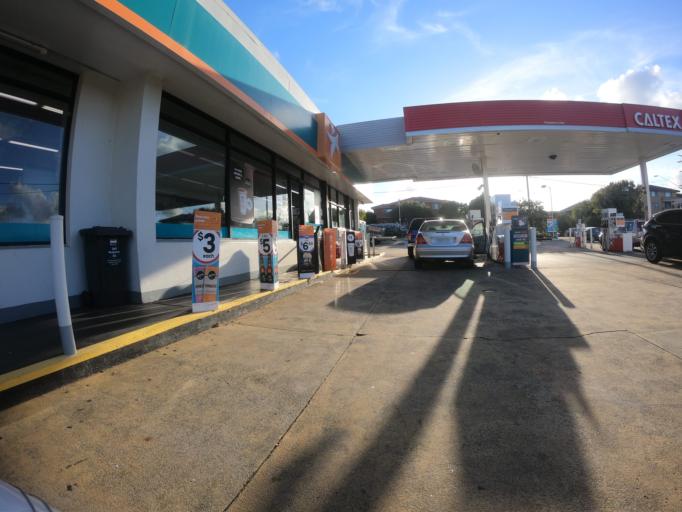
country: AU
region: New South Wales
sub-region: Rockdale
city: Brighton-Le-Sands
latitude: -33.9652
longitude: 151.1412
